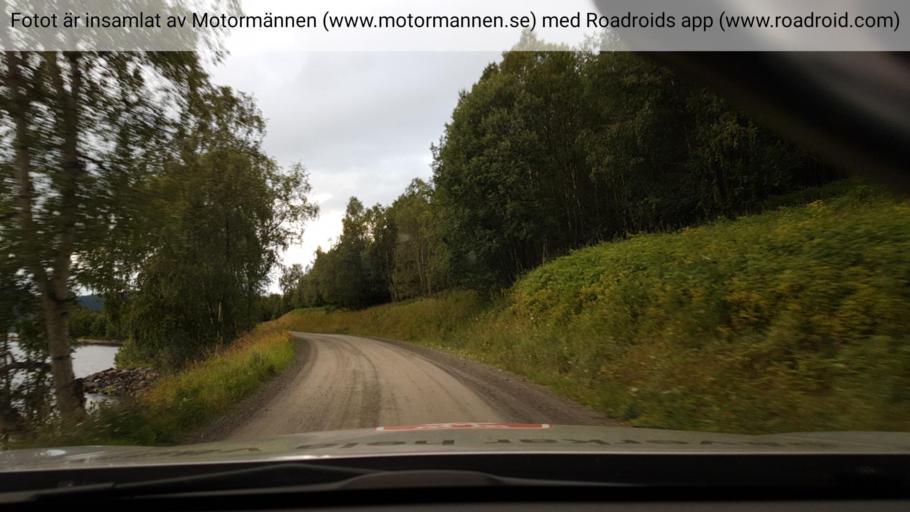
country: NO
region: Nordland
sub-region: Hattfjelldal
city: Hattfjelldal
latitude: 65.6419
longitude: 15.1992
